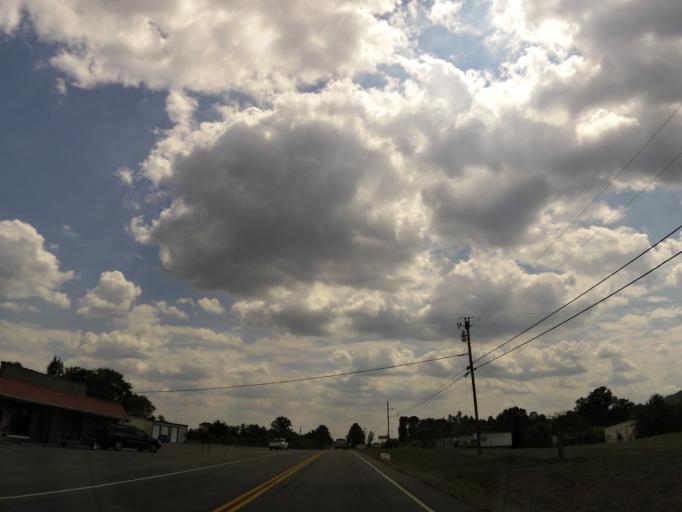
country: US
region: Tennessee
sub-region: Sequatchie County
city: Dunlap
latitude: 35.4404
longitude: -85.3467
